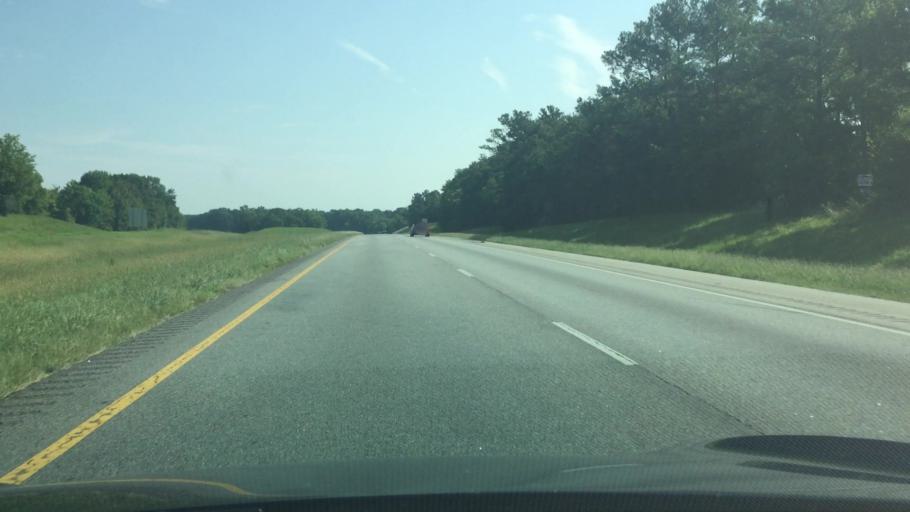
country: US
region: Alabama
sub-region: Lowndes County
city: Hayneville
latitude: 32.1161
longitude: -86.4553
